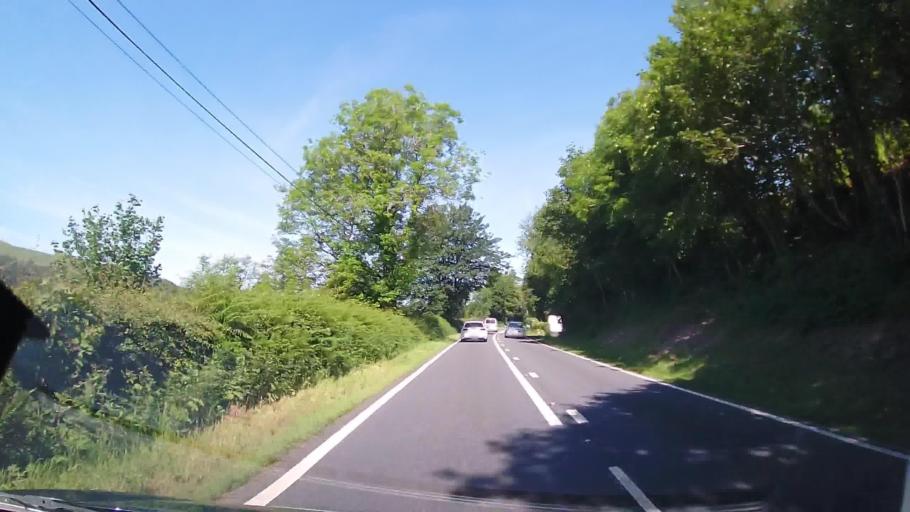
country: GB
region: Wales
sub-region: Sir Powys
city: Llangynog
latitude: 52.6976
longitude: -3.5209
